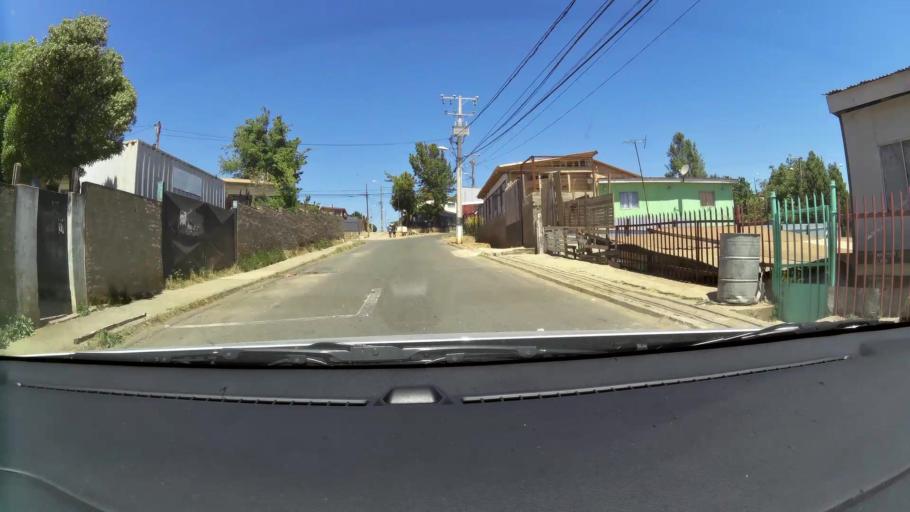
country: CL
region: Valparaiso
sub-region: Provincia de Valparaiso
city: Valparaiso
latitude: -33.0553
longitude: -71.6405
